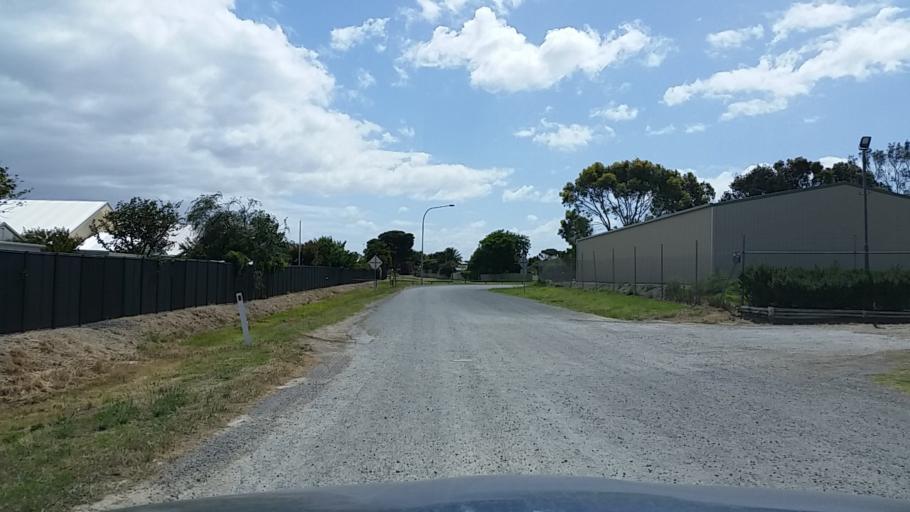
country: AU
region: South Australia
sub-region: Alexandrina
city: Port Elliot
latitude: -35.5252
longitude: 138.6782
